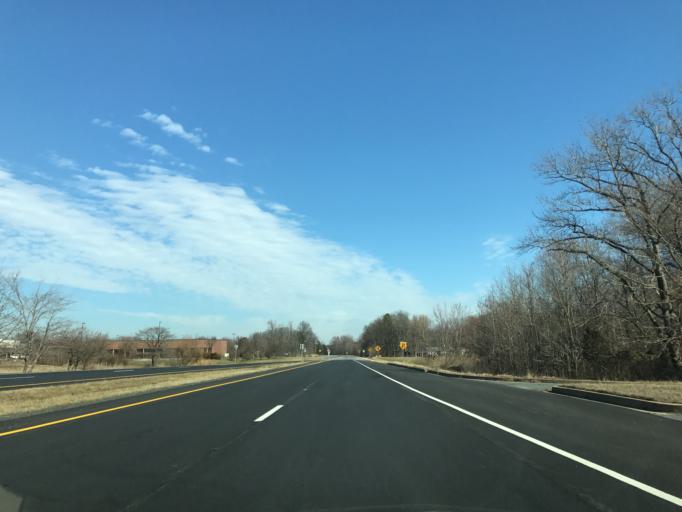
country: US
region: Maryland
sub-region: Queen Anne's County
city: Stevensville
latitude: 38.9837
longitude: -76.3172
